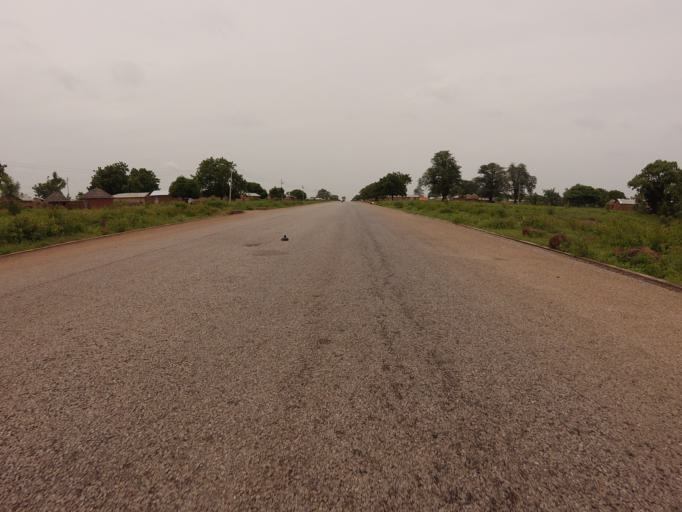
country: GH
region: Northern
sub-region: Yendi
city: Yendi
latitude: 9.3931
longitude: -0.0097
